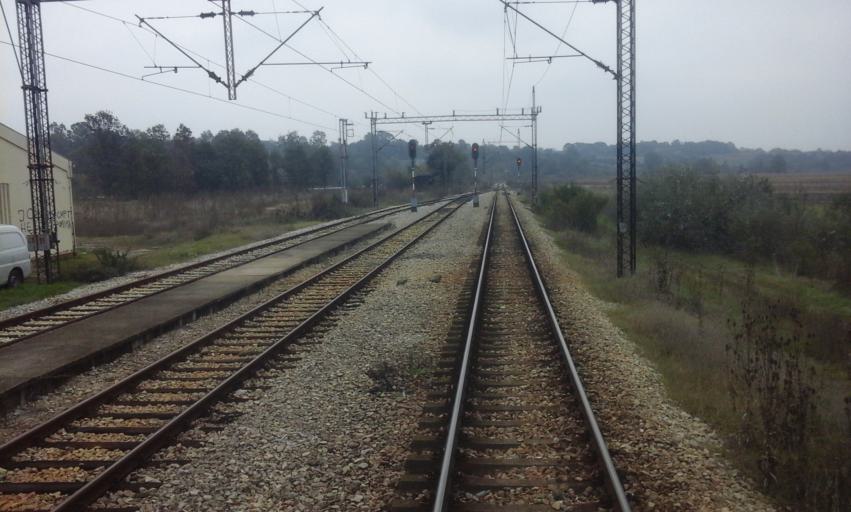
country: RS
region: Central Serbia
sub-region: Belgrade
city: Mladenovac
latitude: 44.3992
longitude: 20.7504
